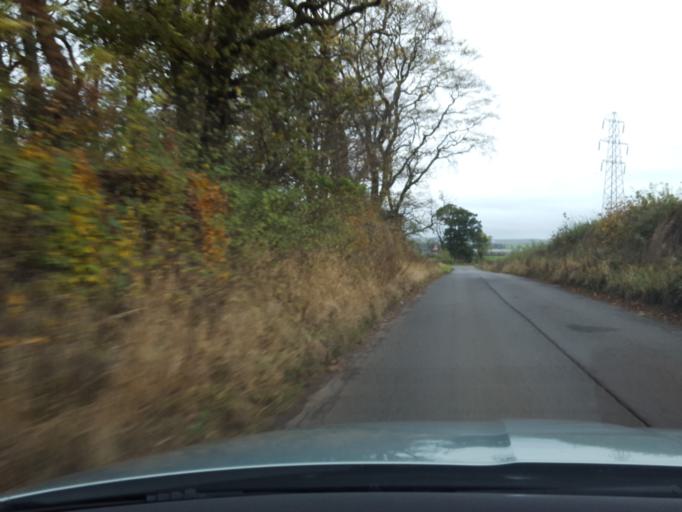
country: GB
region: Scotland
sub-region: West Lothian
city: Kirknewton
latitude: 55.9081
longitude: -3.4366
